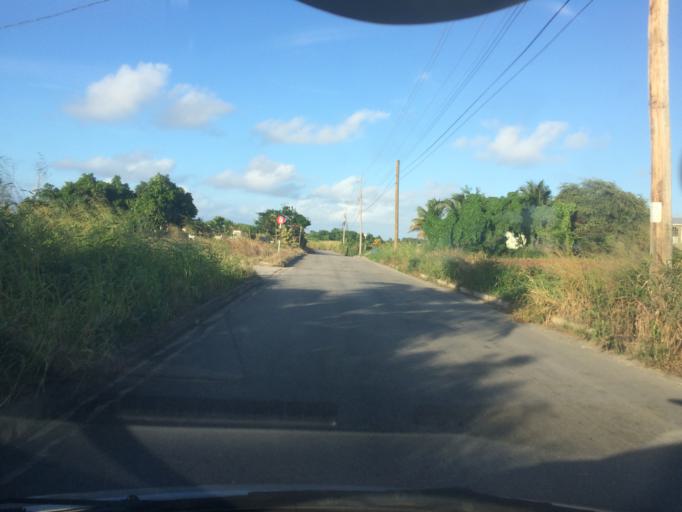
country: BB
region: Saint Lucy
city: Checker Hall
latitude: 13.3066
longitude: -59.6394
